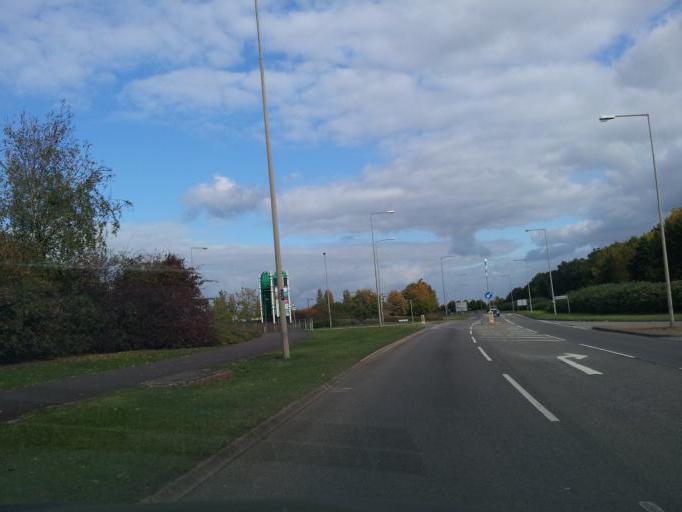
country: GB
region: England
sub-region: Milton Keynes
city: Shenley Church End
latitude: 52.0028
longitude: -0.7933
